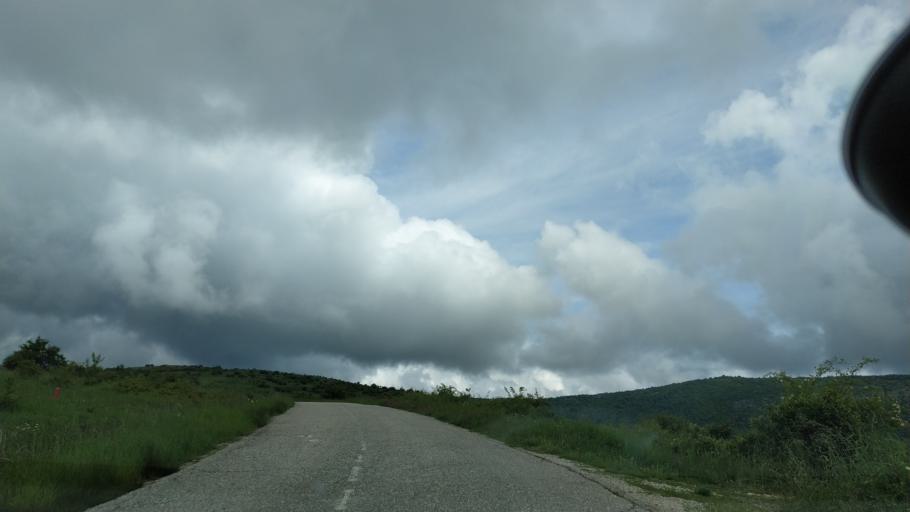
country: RS
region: Central Serbia
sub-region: Zajecarski Okrug
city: Soko Banja
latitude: 43.7040
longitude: 21.9375
